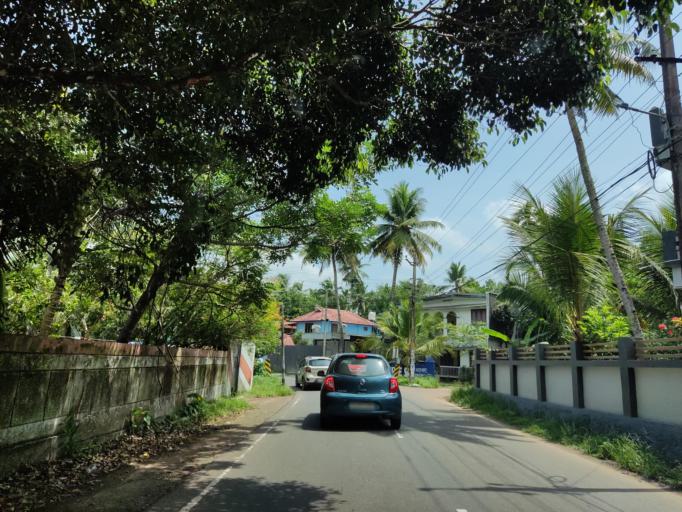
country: IN
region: Kerala
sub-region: Alappuzha
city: Chengannur
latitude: 9.3032
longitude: 76.5871
